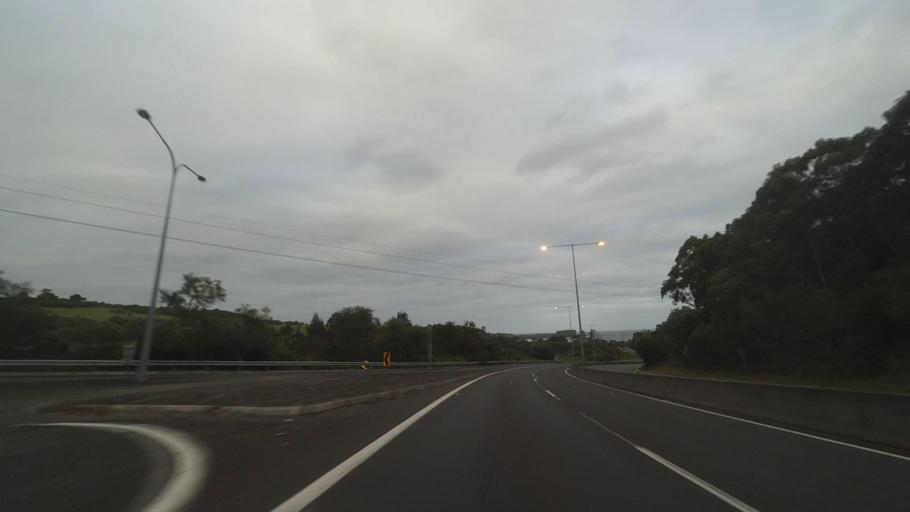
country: AU
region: New South Wales
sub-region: Kiama
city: Kiama
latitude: -34.6626
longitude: 150.8483
